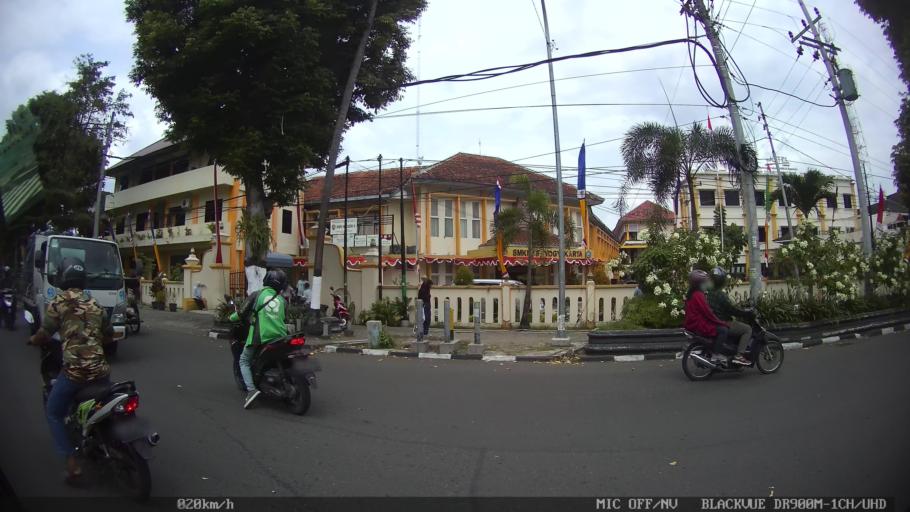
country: ID
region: Daerah Istimewa Yogyakarta
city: Yogyakarta
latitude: -7.7973
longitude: 110.3824
